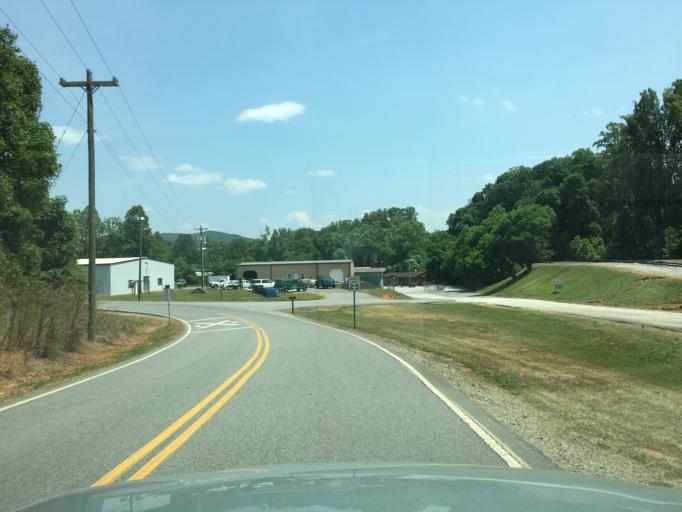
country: US
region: North Carolina
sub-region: McDowell County
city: Marion
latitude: 35.6543
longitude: -81.9619
